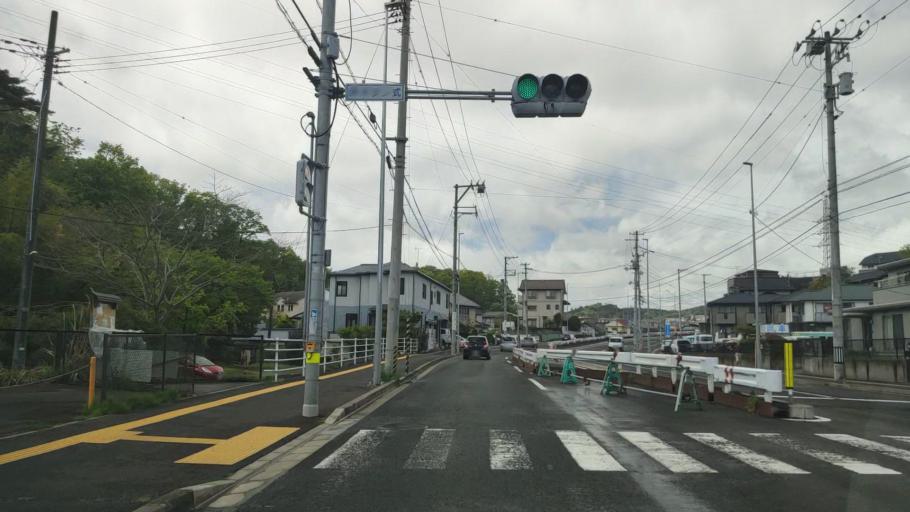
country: JP
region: Miyagi
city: Sendai
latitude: 38.2265
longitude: 140.8602
